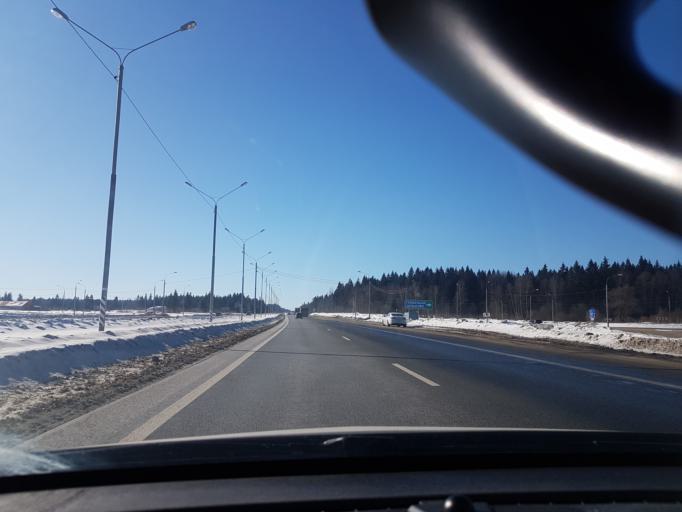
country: RU
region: Moskovskaya
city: Sychevo
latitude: 55.9851
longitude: 36.3369
